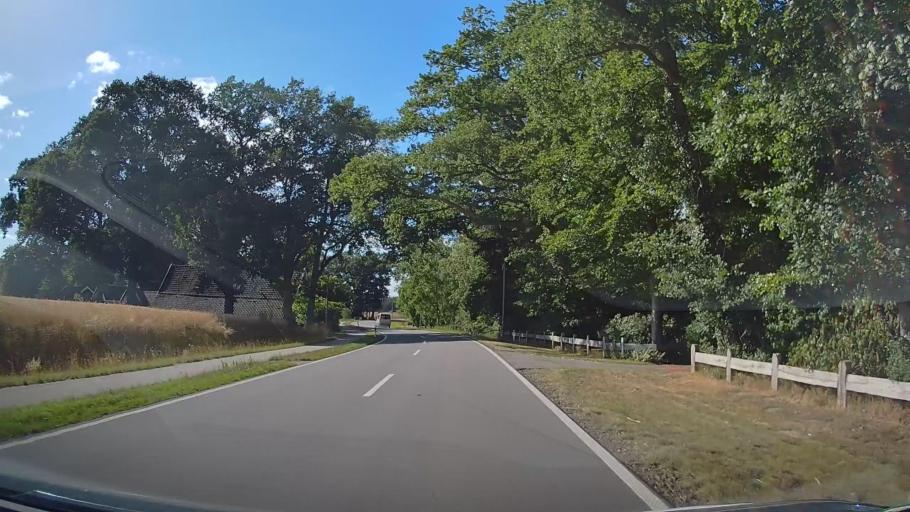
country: DE
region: Lower Saxony
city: Loningen
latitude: 52.6930
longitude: 7.7641
